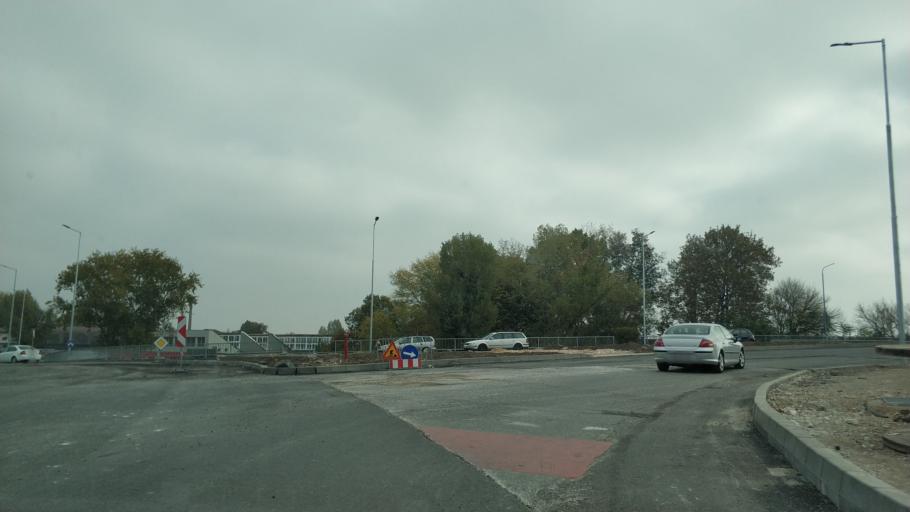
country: BG
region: Plovdiv
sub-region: Obshtina Plovdiv
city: Plovdiv
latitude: 42.1599
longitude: 24.7645
